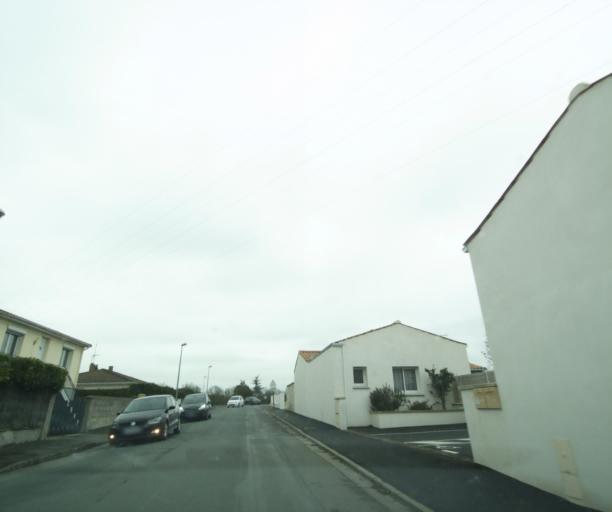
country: FR
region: Poitou-Charentes
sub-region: Departement de la Charente-Maritime
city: Lagord
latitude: 46.1822
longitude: -1.1402
